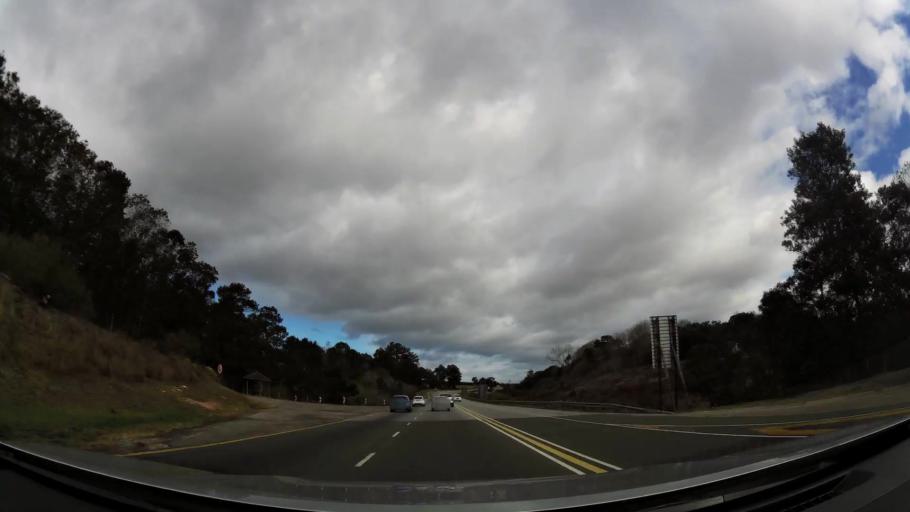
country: ZA
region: Western Cape
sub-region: Eden District Municipality
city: George
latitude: -33.9915
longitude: 22.5359
